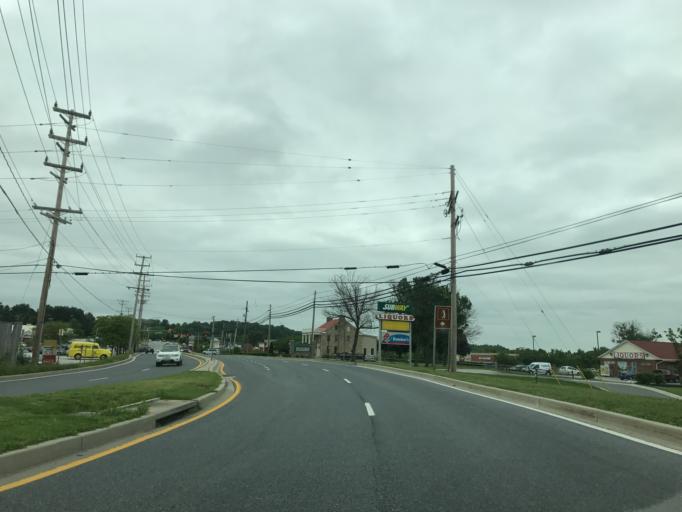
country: US
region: Maryland
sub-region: Carroll County
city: Manchester
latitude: 39.6361
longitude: -76.8659
